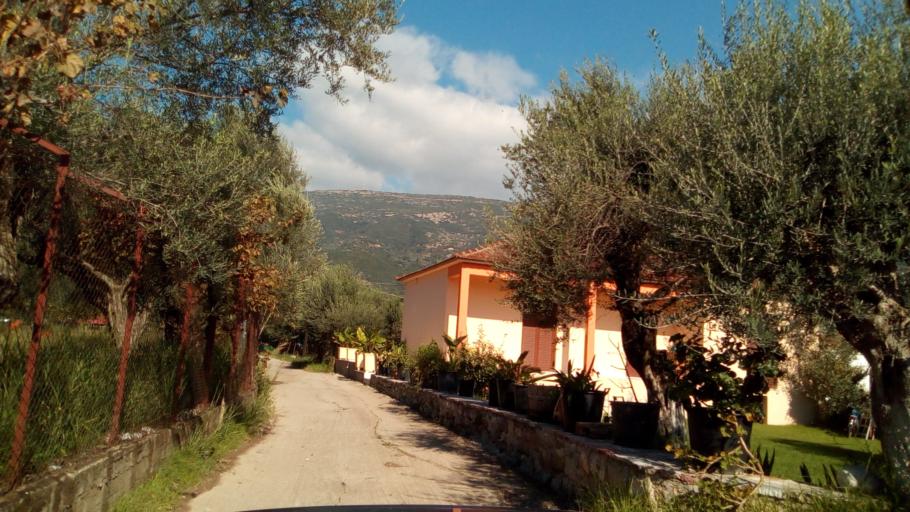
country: GR
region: West Greece
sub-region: Nomos Aitolias kai Akarnanias
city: Nafpaktos
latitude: 38.3903
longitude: 21.8119
